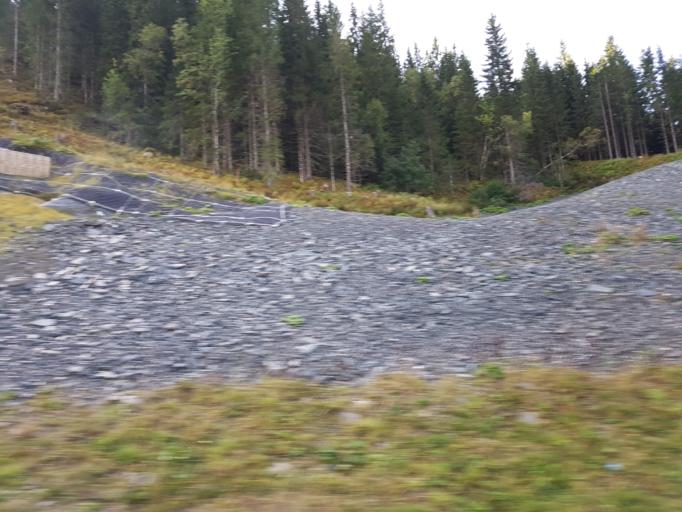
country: NO
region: Sor-Trondelag
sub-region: Rissa
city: Rissa
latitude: 63.6697
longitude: 10.2175
